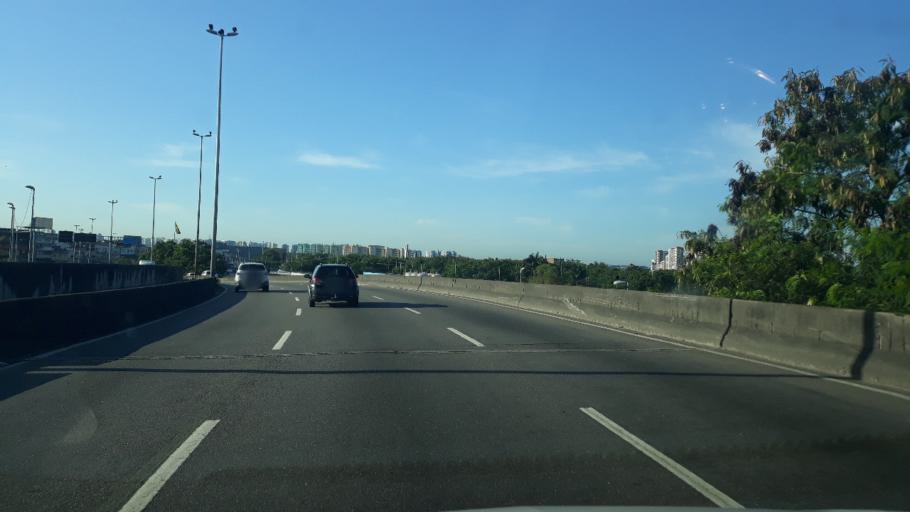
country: BR
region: Rio de Janeiro
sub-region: Sao Joao De Meriti
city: Sao Joao de Meriti
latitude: -22.9541
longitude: -43.3574
